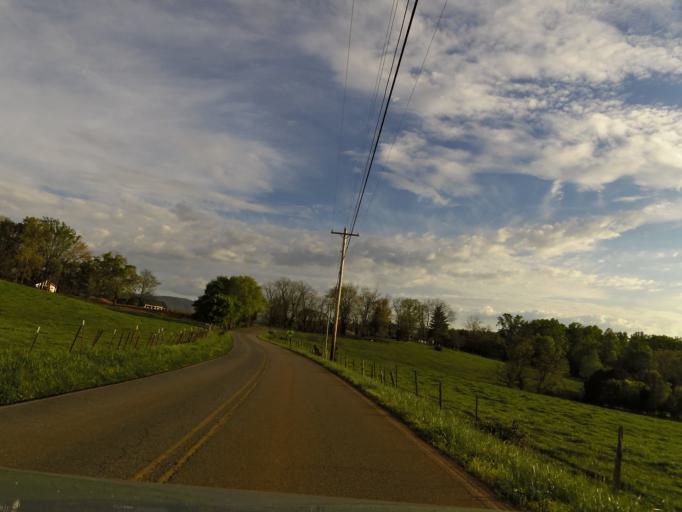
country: US
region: Tennessee
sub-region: Blount County
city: Maryville
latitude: 35.6707
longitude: -84.0185
